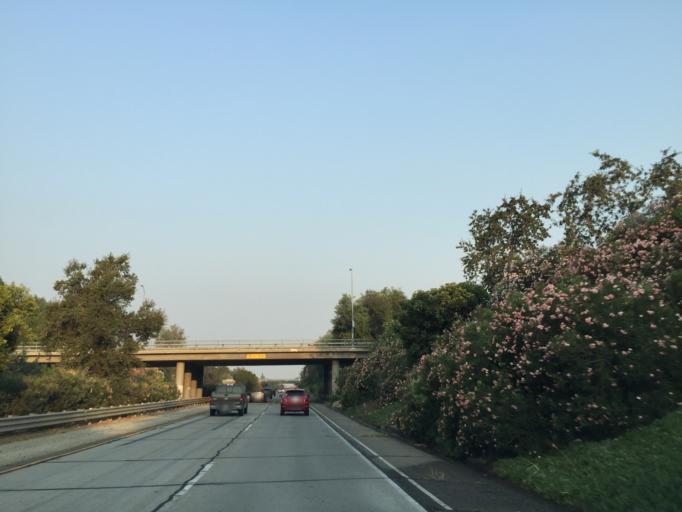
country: US
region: California
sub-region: Tulare County
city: Visalia
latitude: 36.3271
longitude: -119.2924
